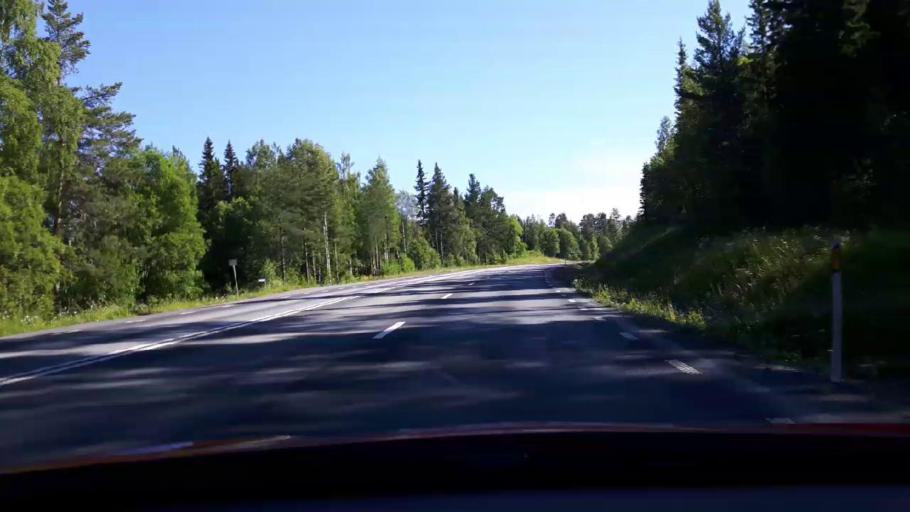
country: SE
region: Jaemtland
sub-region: OEstersunds Kommun
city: Ostersund
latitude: 63.2068
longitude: 14.6842
